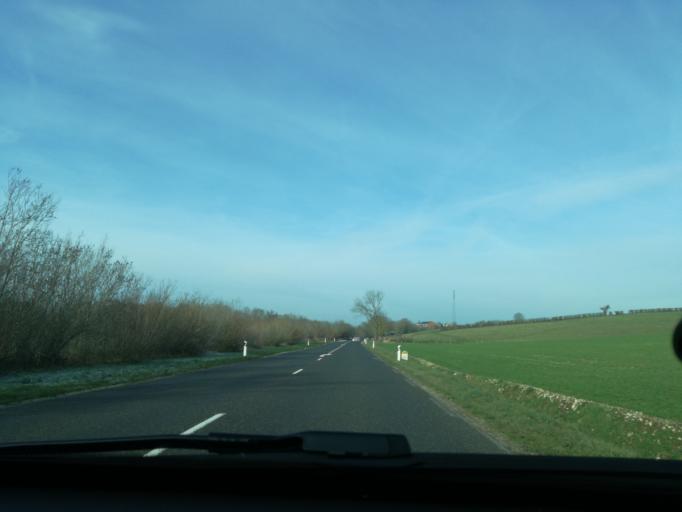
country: FR
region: Lorraine
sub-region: Departement de la Meuse
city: Fains-Veel
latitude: 48.8019
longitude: 5.1181
